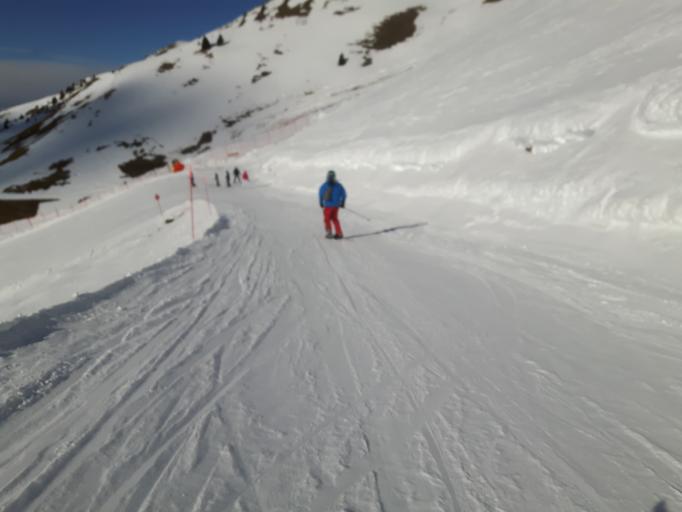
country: IT
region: Trentino-Alto Adige
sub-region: Provincia di Trento
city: Predazzo
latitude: 46.3494
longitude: 11.5533
